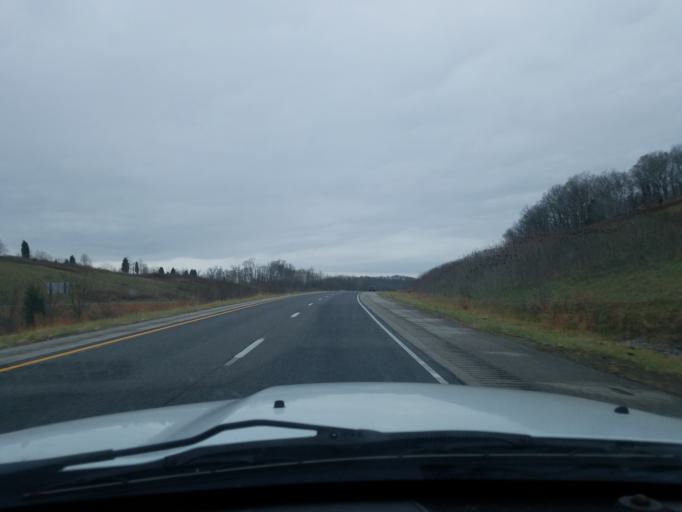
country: US
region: Indiana
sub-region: Dubois County
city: Ferdinand
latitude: 38.2179
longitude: -86.7260
